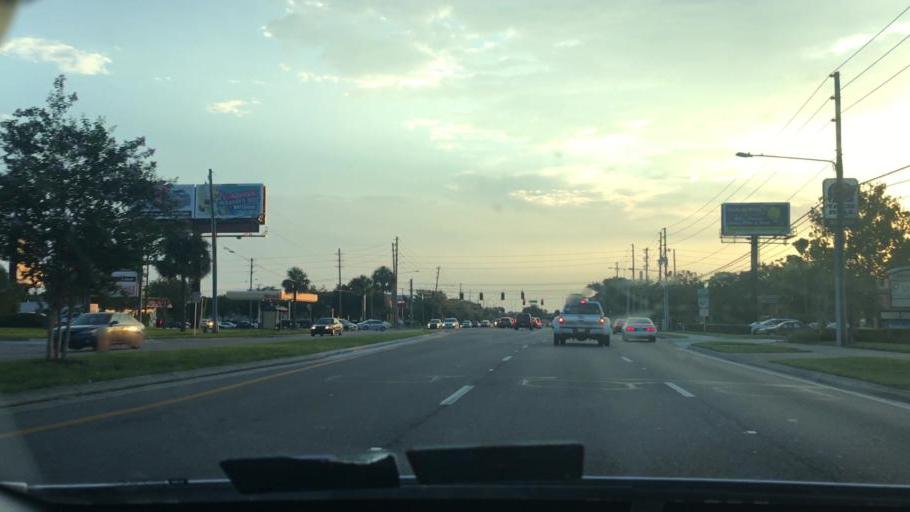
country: US
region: Florida
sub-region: Orange County
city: Alafaya
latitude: 28.5976
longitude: -81.2429
